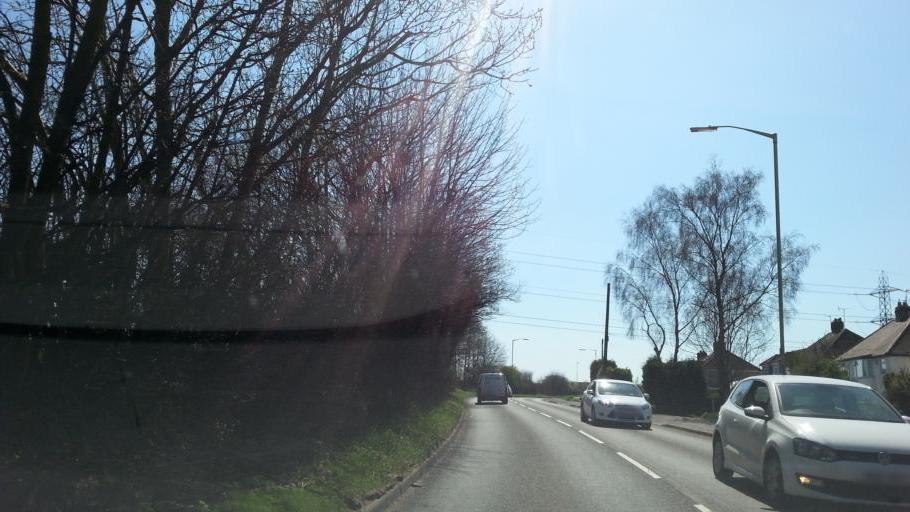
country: GB
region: England
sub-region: Staffordshire
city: Cannock
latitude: 52.6727
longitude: -2.0509
